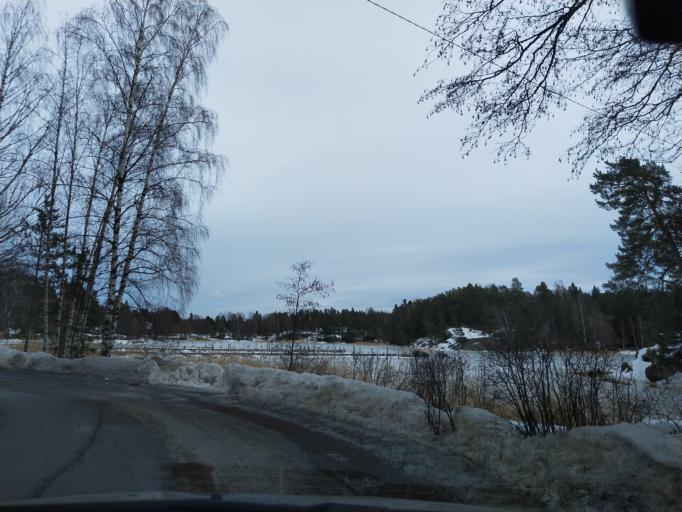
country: FI
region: Uusimaa
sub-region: Helsinki
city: Sibbo
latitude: 60.2561
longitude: 25.3015
